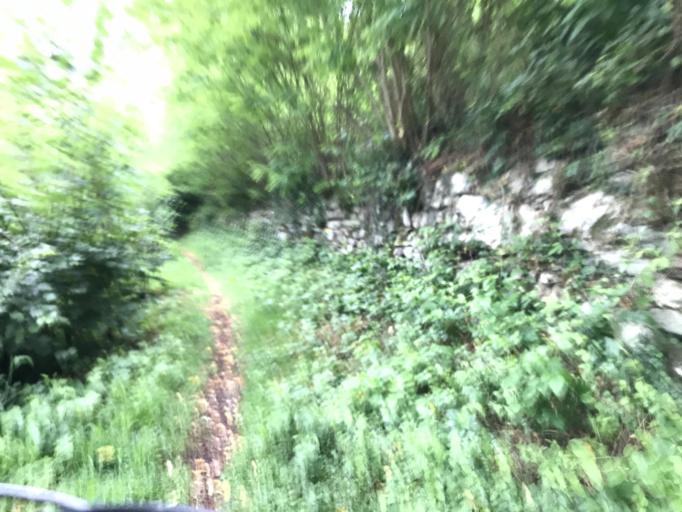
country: IT
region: Lombardy
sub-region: Provincia di Varese
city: Brenta
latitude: 45.8991
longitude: 8.6883
